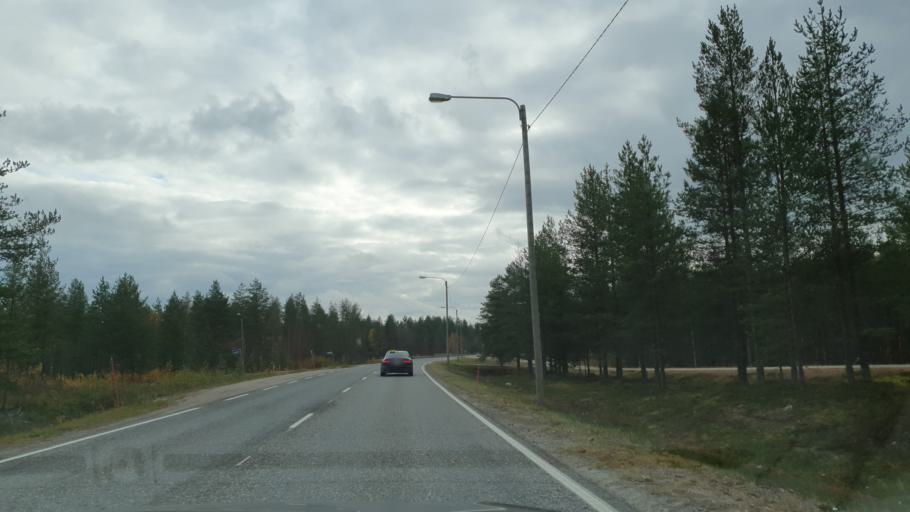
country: FI
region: Northern Ostrobothnia
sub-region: Oulunkaari
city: Pudasjaervi
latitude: 65.3855
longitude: 26.9875
